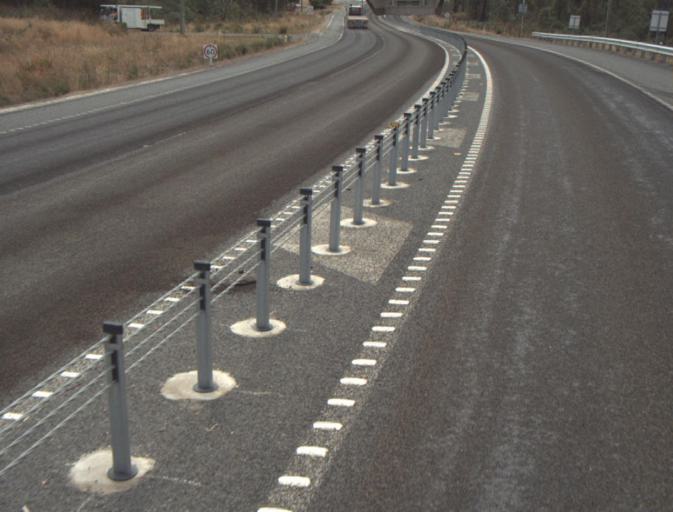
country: AU
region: Tasmania
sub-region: Launceston
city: Mayfield
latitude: -41.2969
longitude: 147.0497
